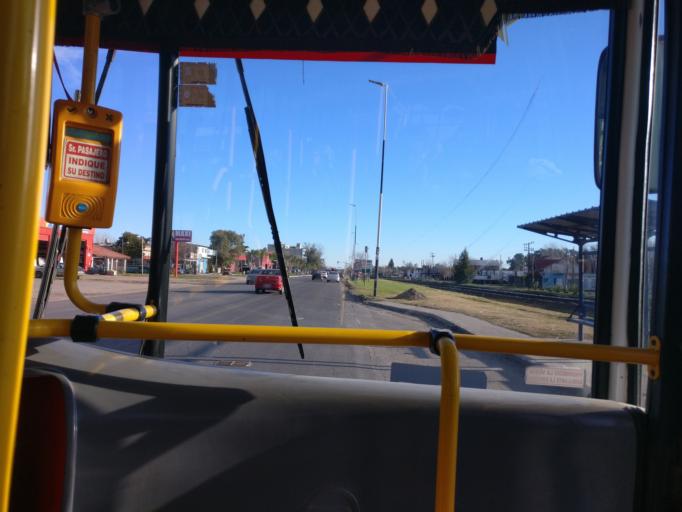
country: AR
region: Buenos Aires
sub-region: Partido de Ezeiza
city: Ezeiza
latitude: -34.8785
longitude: -58.5537
